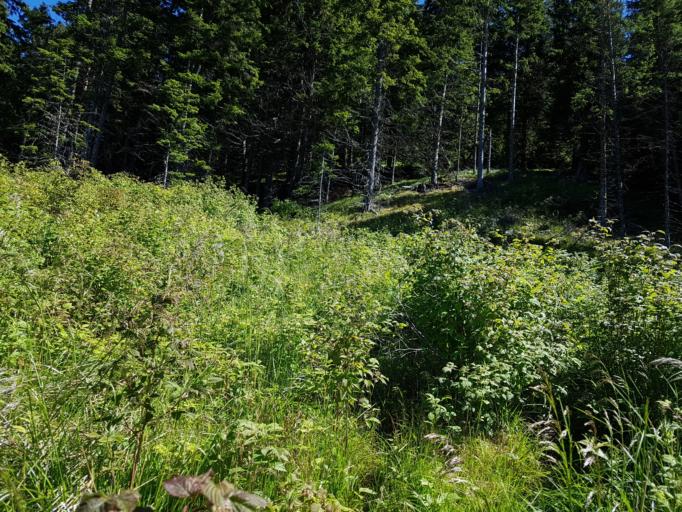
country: NO
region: Sor-Trondelag
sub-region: Skaun
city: Borsa
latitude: 63.4329
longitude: 10.1947
